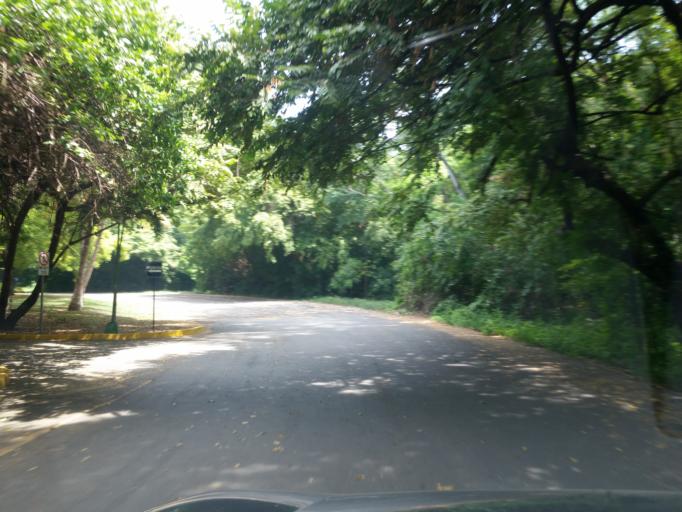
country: NI
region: Managua
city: Masachapa
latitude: 11.8098
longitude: -86.5178
